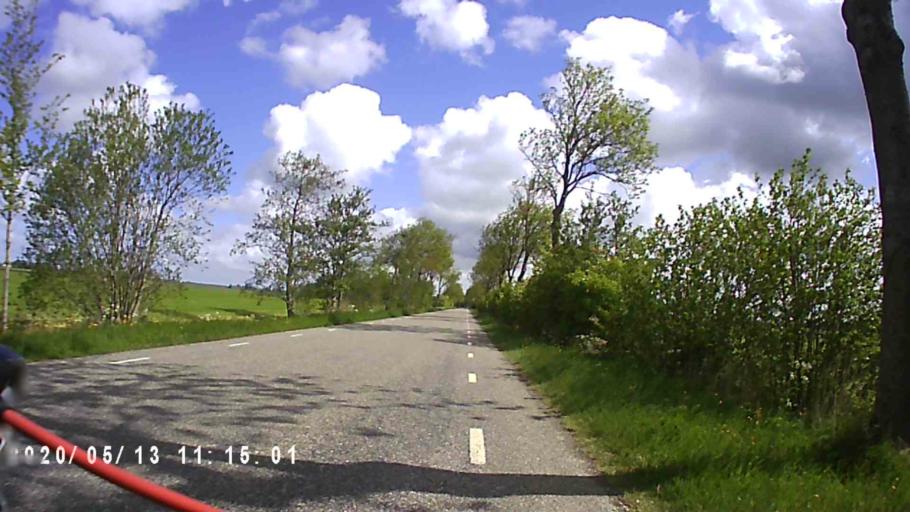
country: NL
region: Groningen
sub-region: Gemeente Zuidhorn
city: Oldehove
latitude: 53.3019
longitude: 6.3641
